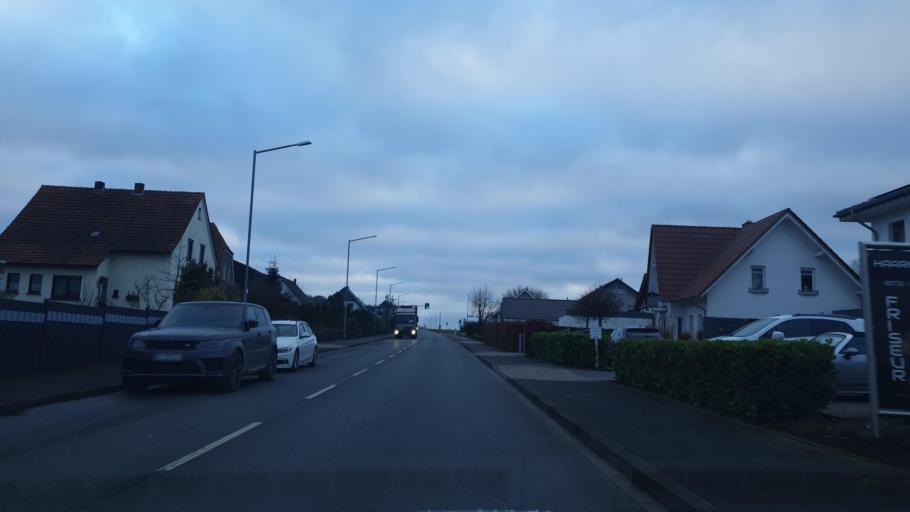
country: DE
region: North Rhine-Westphalia
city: Loehne
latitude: 52.1789
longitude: 8.6877
